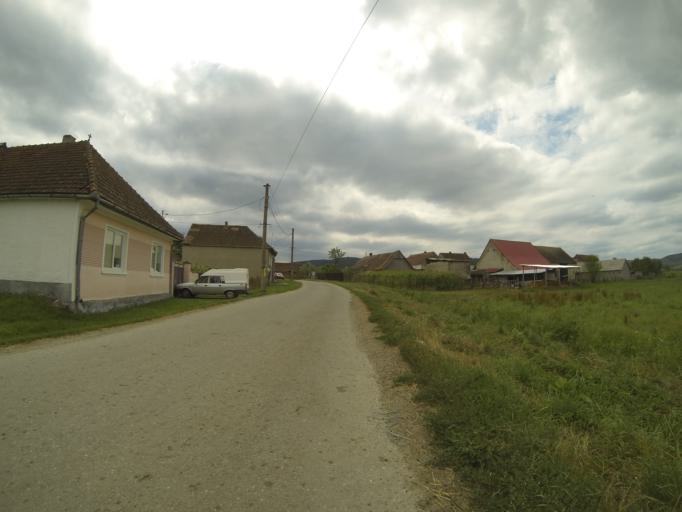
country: RO
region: Brasov
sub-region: Comuna Hoghiz
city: Hoghiz
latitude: 46.0219
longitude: 25.3781
